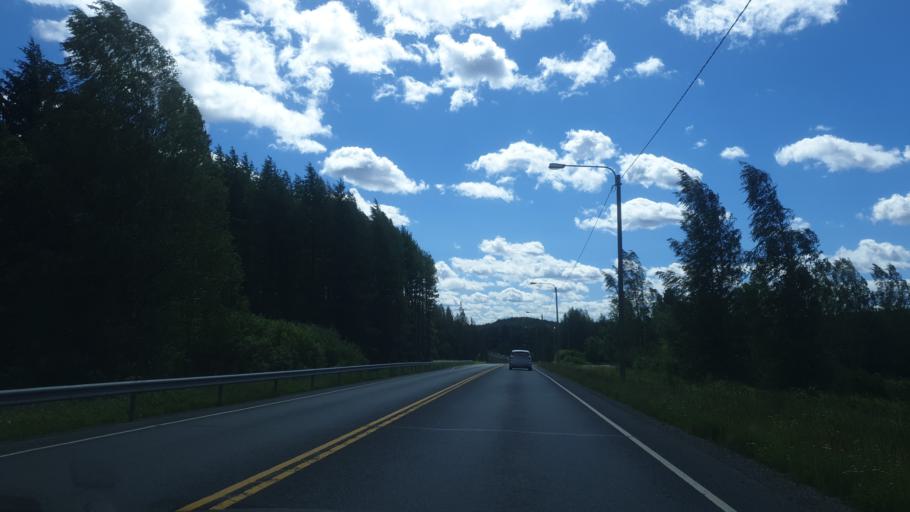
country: FI
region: Northern Savo
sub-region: Varkaus
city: Leppaevirta
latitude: 62.6424
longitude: 27.6084
